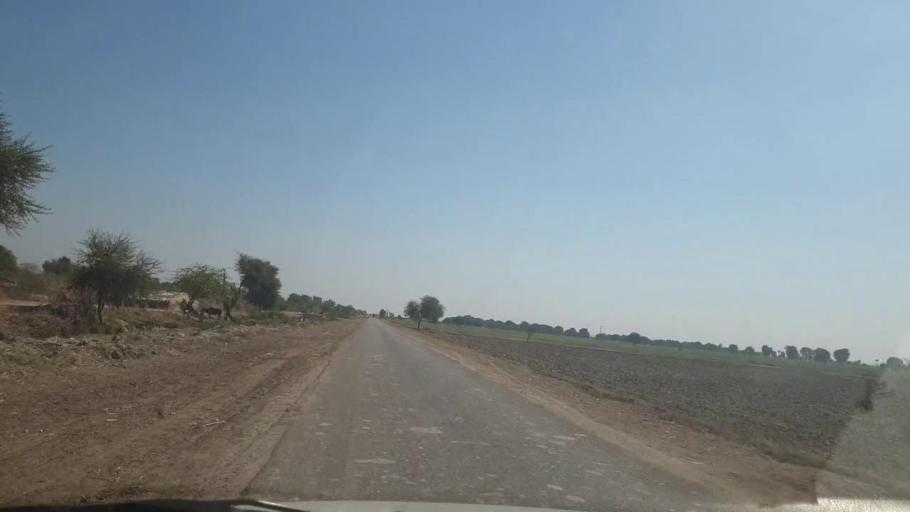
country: PK
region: Sindh
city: Mirpur Khas
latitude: 25.4682
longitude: 69.1777
